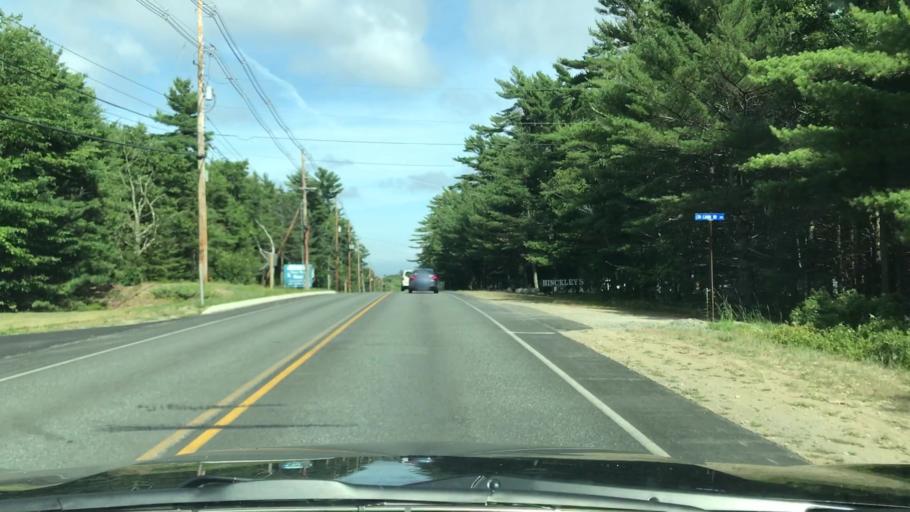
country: US
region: Maine
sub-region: Hancock County
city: Bar Harbor
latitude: 44.4304
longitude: -68.2642
